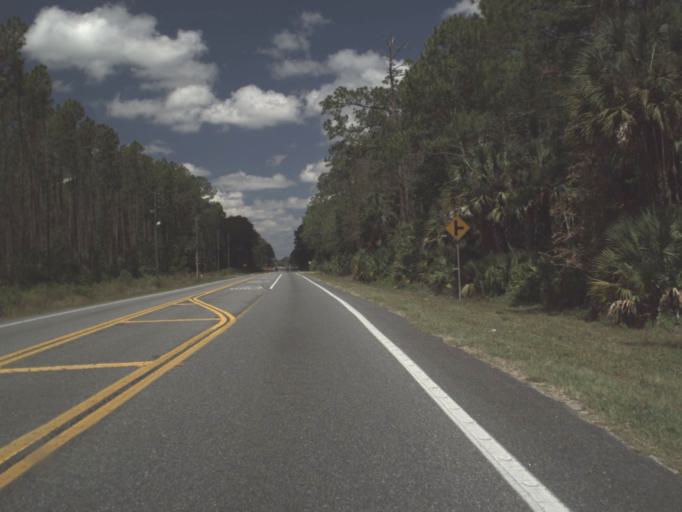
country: US
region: Florida
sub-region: Marion County
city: Silver Springs Shores
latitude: 29.2126
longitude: -81.9561
